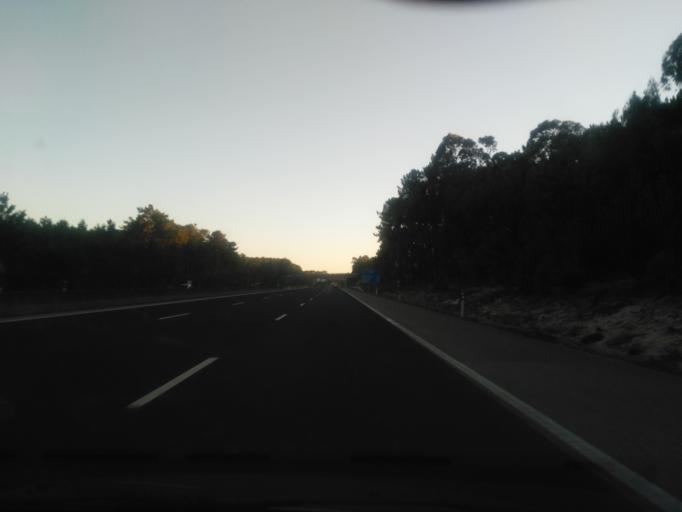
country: PT
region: Leiria
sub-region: Leiria
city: Maceira
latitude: 39.7064
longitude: -8.9194
